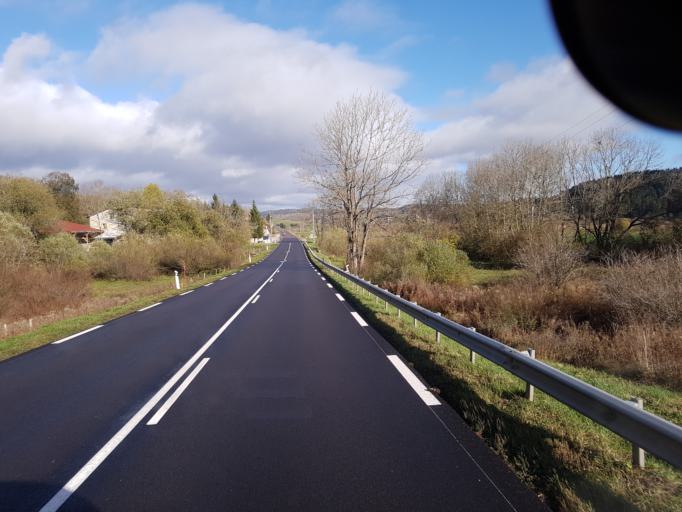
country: FR
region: Franche-Comte
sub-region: Departement du Jura
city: Morbier
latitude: 46.5984
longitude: 5.9600
